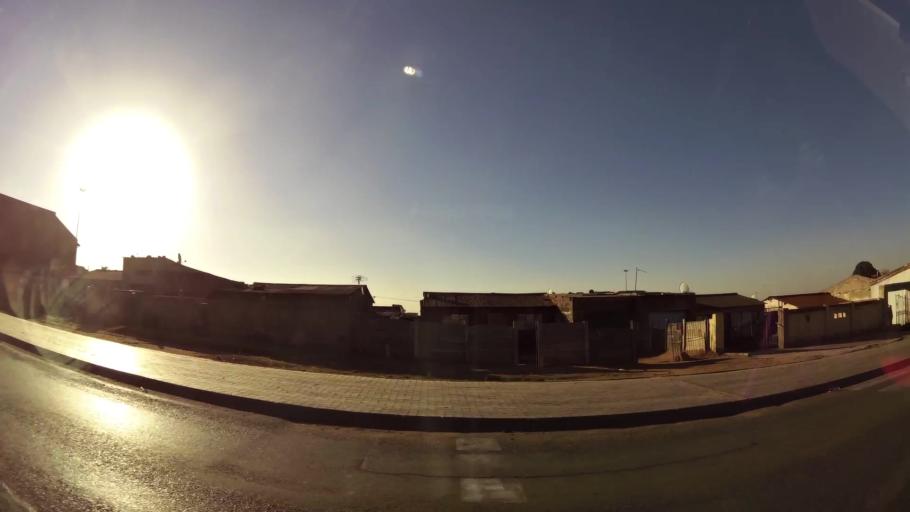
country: ZA
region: Gauteng
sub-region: Ekurhuleni Metropolitan Municipality
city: Tembisa
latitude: -26.0162
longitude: 28.2344
